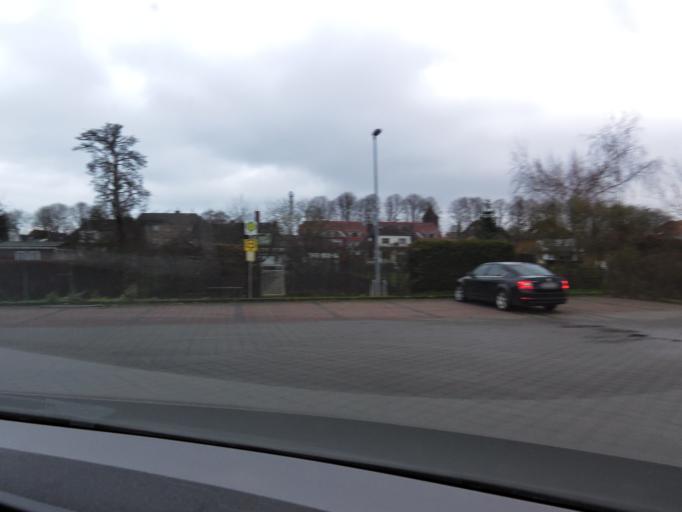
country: DE
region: Mecklenburg-Vorpommern
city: Grevesmuhlen
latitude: 53.8644
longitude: 11.1792
